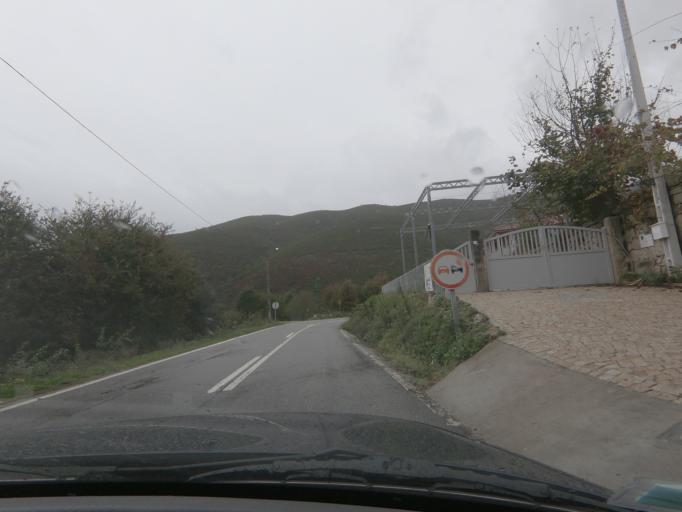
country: PT
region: Vila Real
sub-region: Mondim de Basto
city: Mondim de Basto
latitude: 41.3519
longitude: -7.8849
